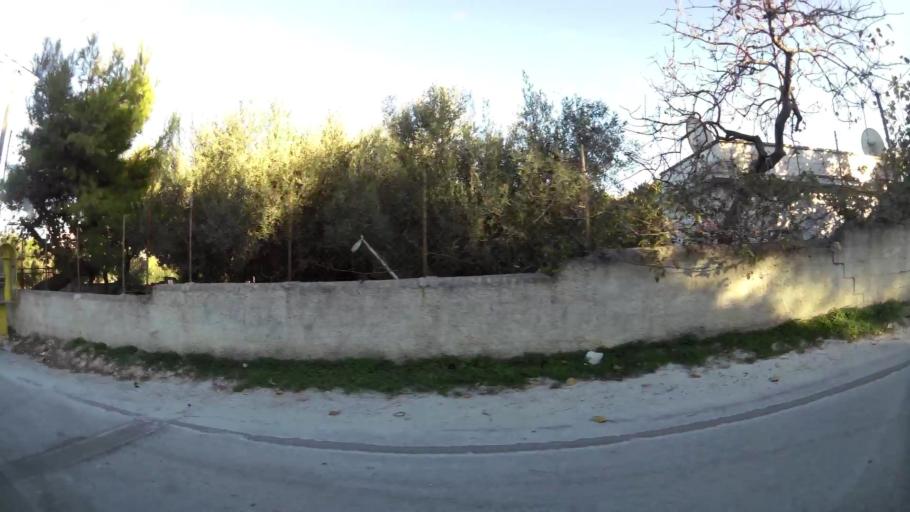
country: GR
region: Attica
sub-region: Nomarchia Anatolikis Attikis
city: Rafina
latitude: 38.0142
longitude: 24.0120
